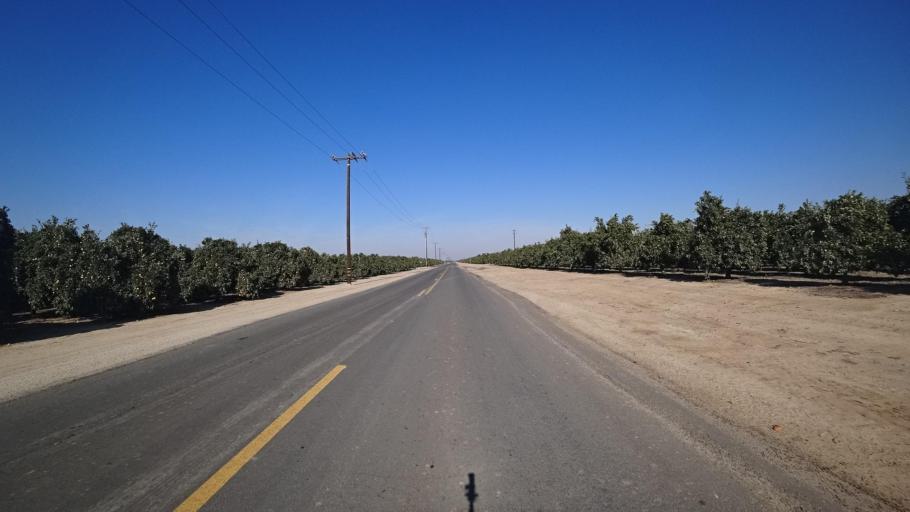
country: US
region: California
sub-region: Tulare County
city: Richgrove
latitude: 35.7242
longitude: -119.1340
